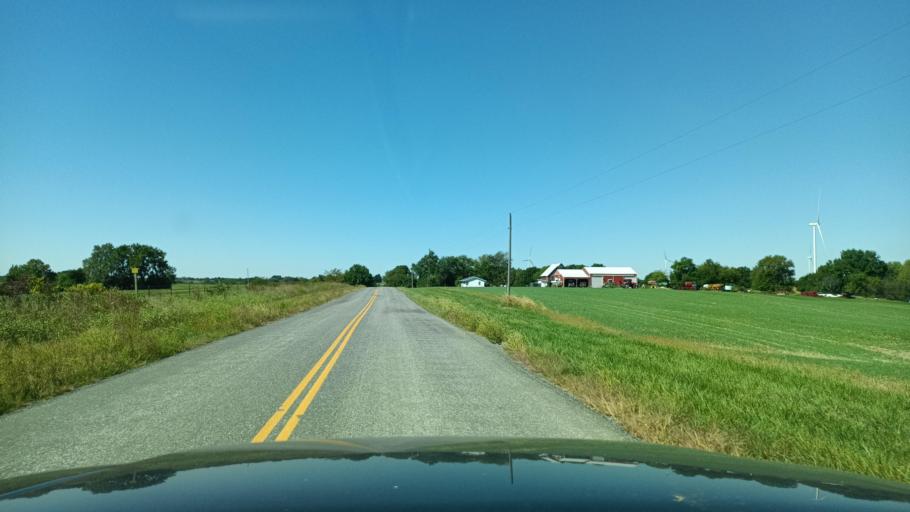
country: US
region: Missouri
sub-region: Adair County
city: Kirksville
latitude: 40.3306
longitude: -92.4995
